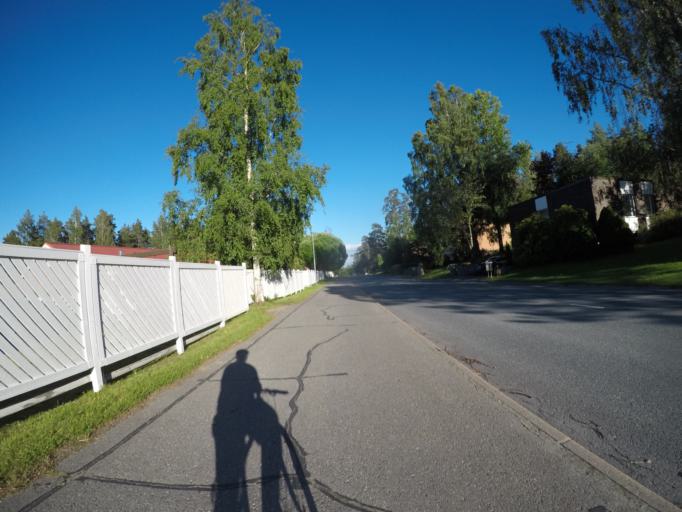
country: FI
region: Haeme
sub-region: Haemeenlinna
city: Haemeenlinna
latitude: 60.9815
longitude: 24.4557
